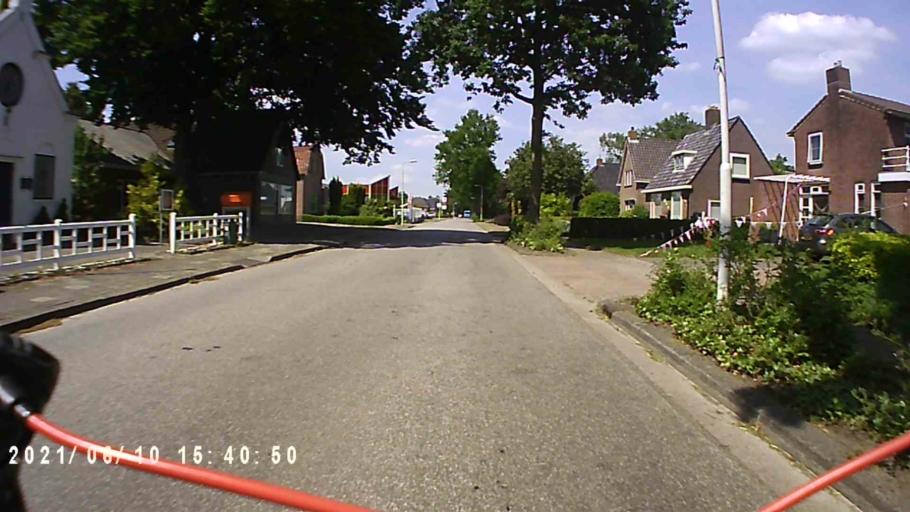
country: NL
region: Friesland
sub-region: Gemeente Achtkarspelen
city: Boelenslaan
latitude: 53.1622
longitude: 6.1459
